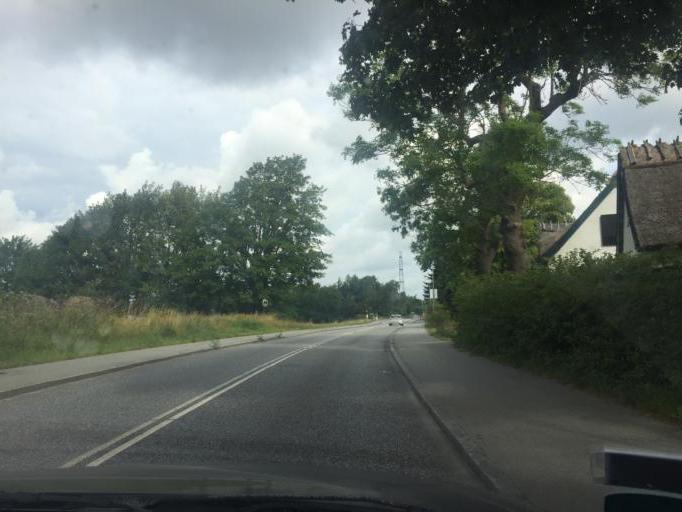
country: DK
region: Capital Region
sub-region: Allerod Kommune
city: Lillerod
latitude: 55.8908
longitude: 12.3524
